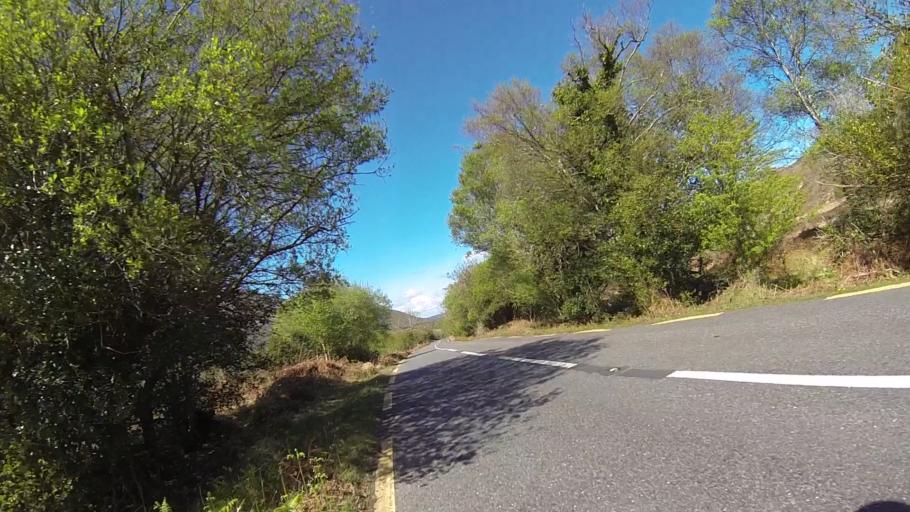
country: IE
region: Munster
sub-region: Ciarrai
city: Cill Airne
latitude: 51.9939
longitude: -9.5510
